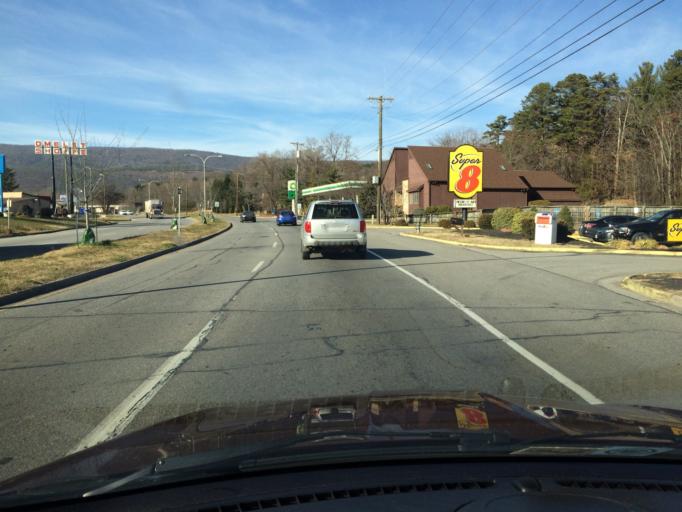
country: US
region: Virginia
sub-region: City of Salem
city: Salem
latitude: 37.2902
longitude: -80.0956
